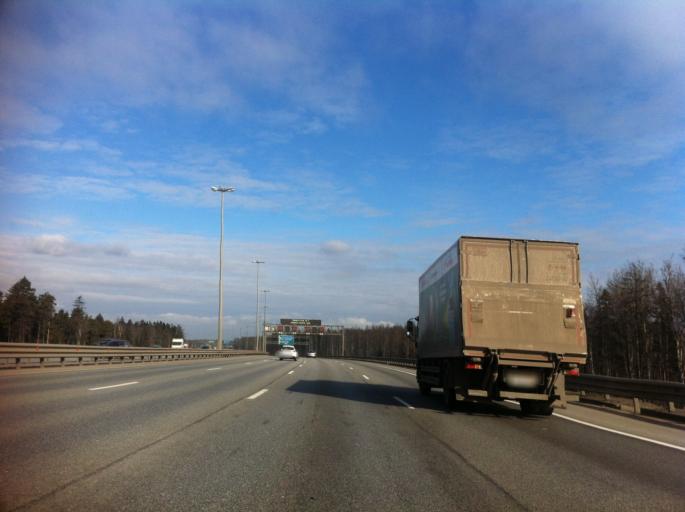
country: RU
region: St.-Petersburg
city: Krasnogvargeisky
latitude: 59.9314
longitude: 30.5369
